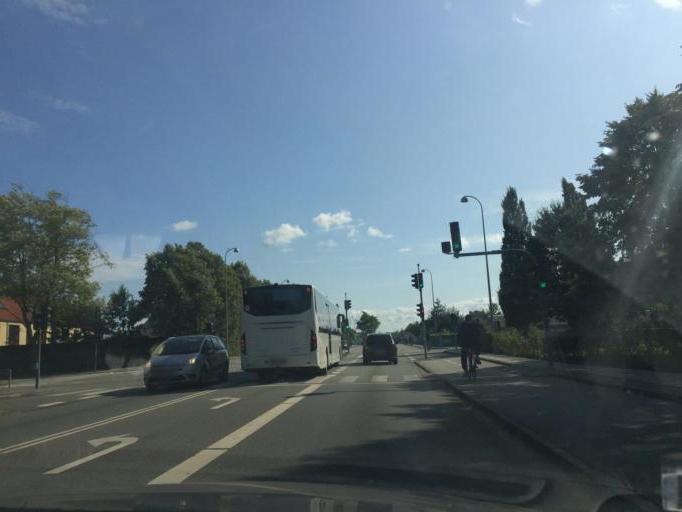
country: DK
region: Capital Region
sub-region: Herlev Kommune
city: Herlev
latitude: 55.7245
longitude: 12.4721
